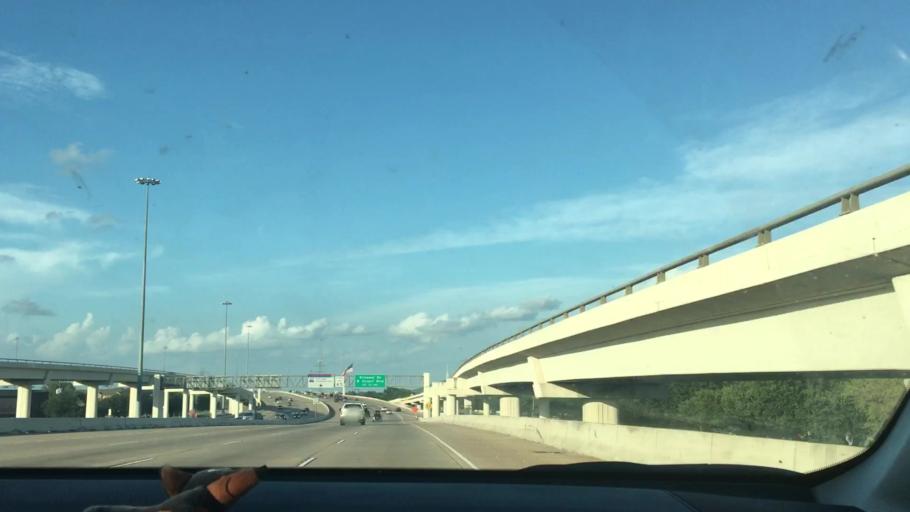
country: US
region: Texas
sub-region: Fort Bend County
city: Meadows Place
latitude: 29.6224
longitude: -95.6002
